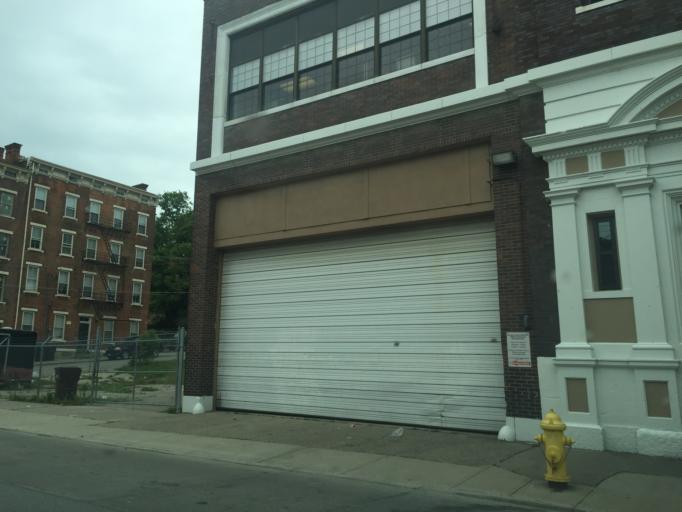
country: US
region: Kentucky
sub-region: Campbell County
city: Newport
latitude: 39.1159
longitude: -84.5158
